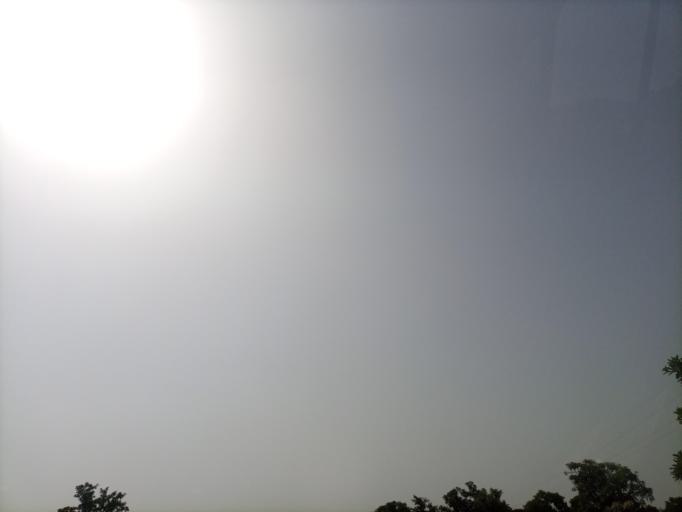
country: GH
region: Northern
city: Savelugu
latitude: 9.5875
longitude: -0.9971
